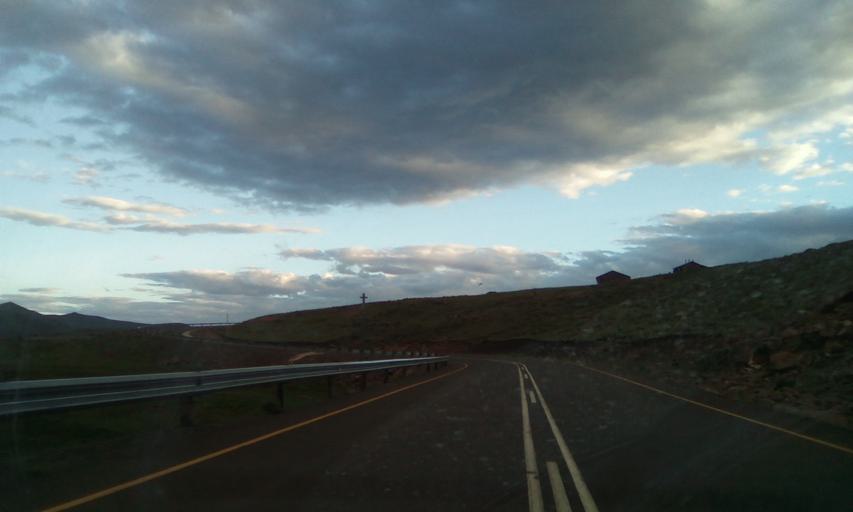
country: LS
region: Maseru
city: Nako
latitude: -29.8155
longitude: 28.0346
